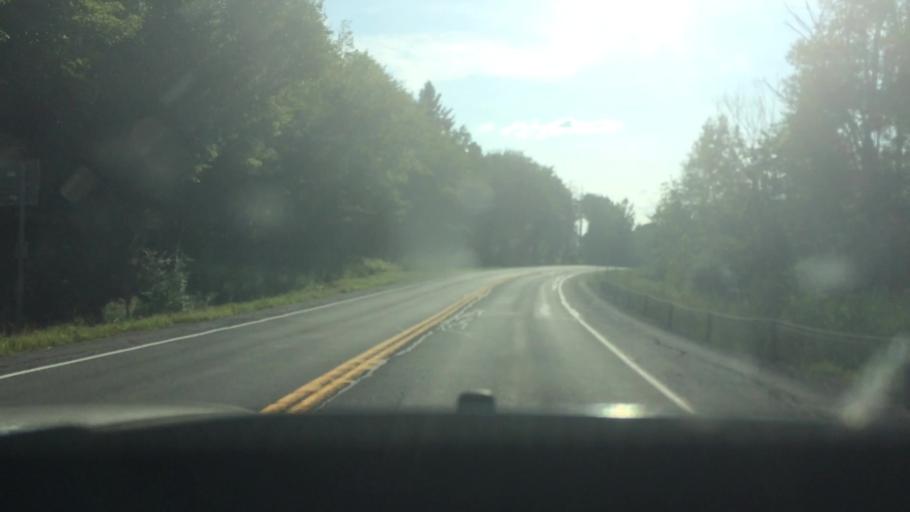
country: US
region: New York
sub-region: St. Lawrence County
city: Potsdam
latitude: 44.6761
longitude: -74.8404
